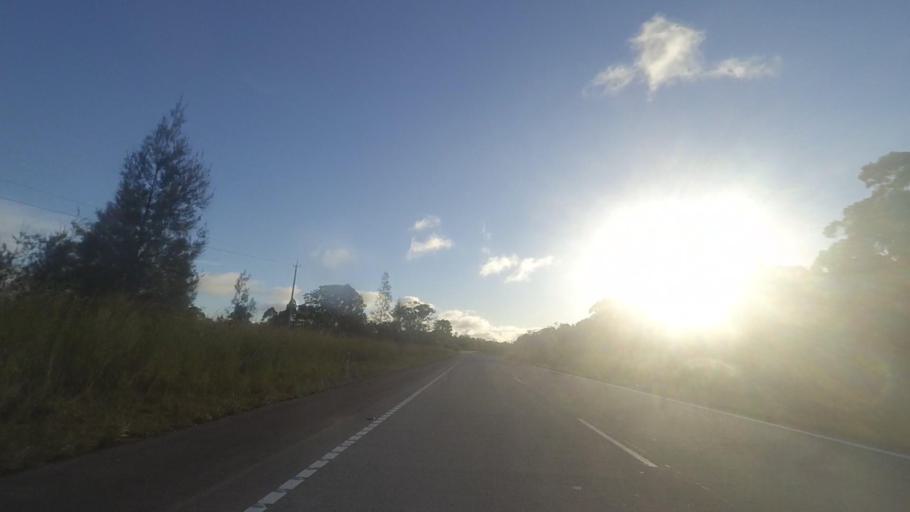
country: AU
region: New South Wales
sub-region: Great Lakes
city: Hawks Nest
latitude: -32.5425
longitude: 152.1653
